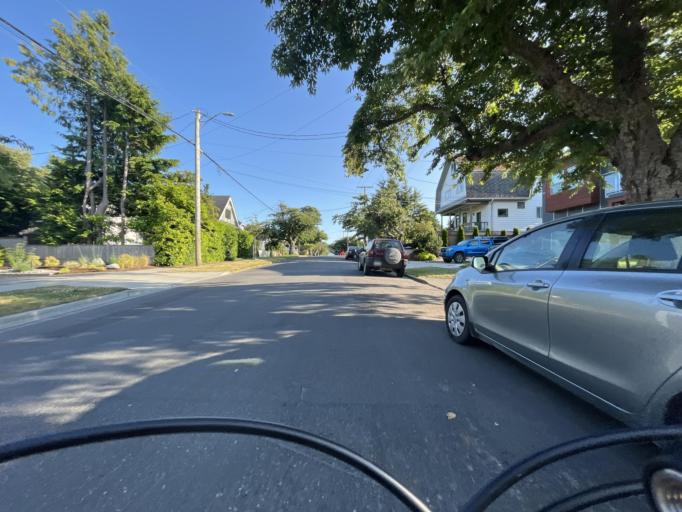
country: CA
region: British Columbia
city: Victoria
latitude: 48.4100
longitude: -123.3501
